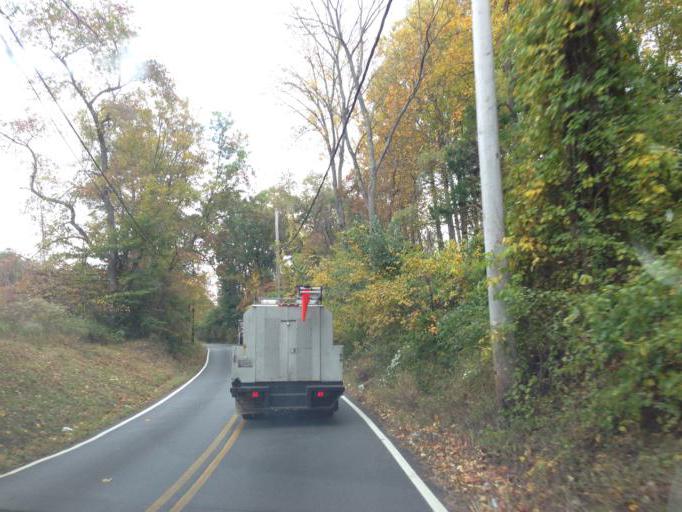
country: US
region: Maryland
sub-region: Baltimore County
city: Milford Mill
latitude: 39.3139
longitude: -76.7861
